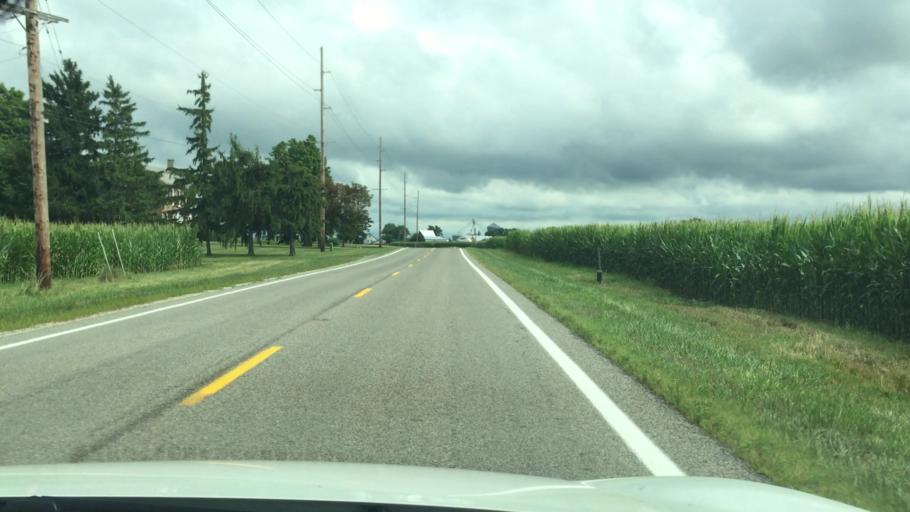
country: US
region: Ohio
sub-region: Champaign County
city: North Lewisburg
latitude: 40.1937
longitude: -83.5254
